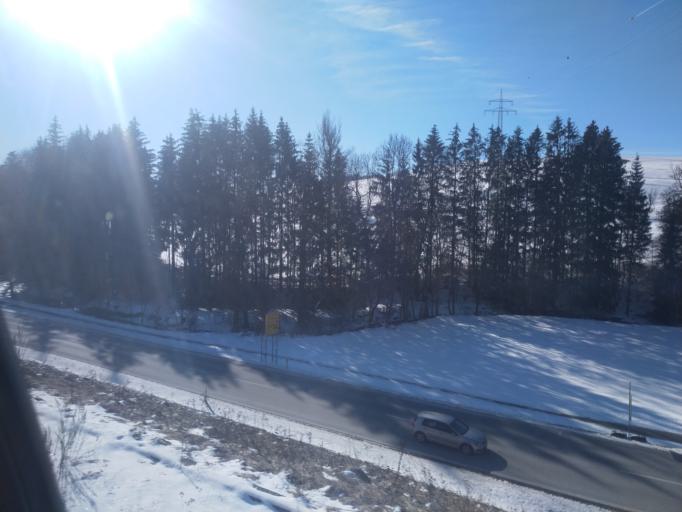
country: DE
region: Baden-Wuerttemberg
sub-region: Freiburg Region
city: Aldingen
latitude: 48.1164
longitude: 8.6889
